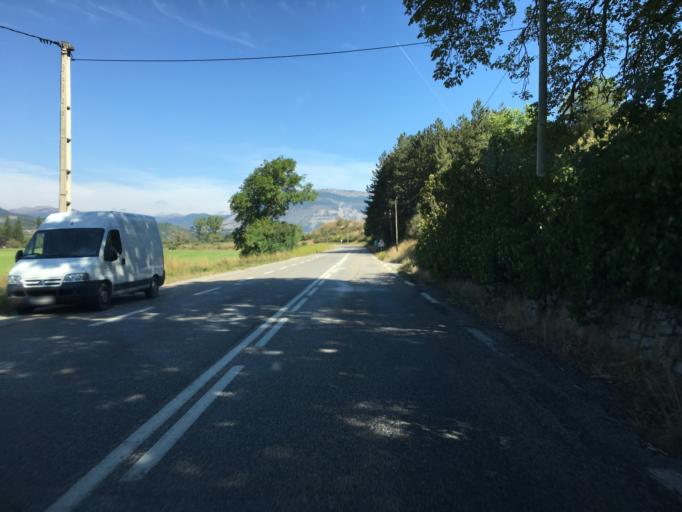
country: FR
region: Provence-Alpes-Cote d'Azur
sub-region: Departement des Hautes-Alpes
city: Serres
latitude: 44.4628
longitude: 5.7259
